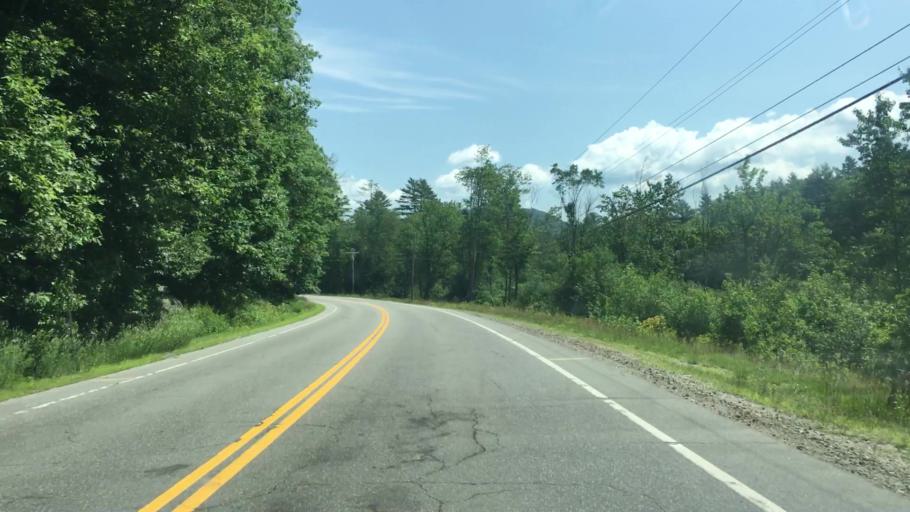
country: US
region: New Hampshire
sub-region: Sullivan County
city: Grantham
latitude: 43.4331
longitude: -72.1602
